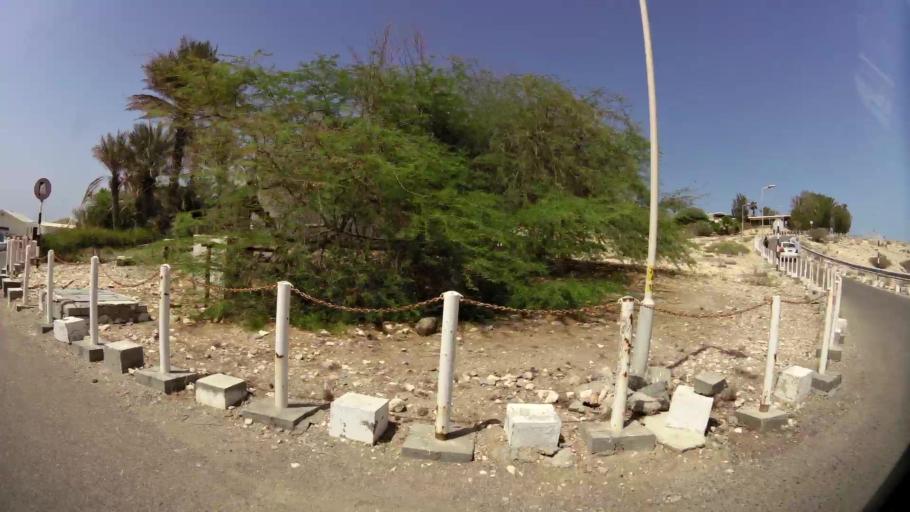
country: OM
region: Muhafazat Masqat
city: Muscat
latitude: 23.6411
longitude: 58.4921
